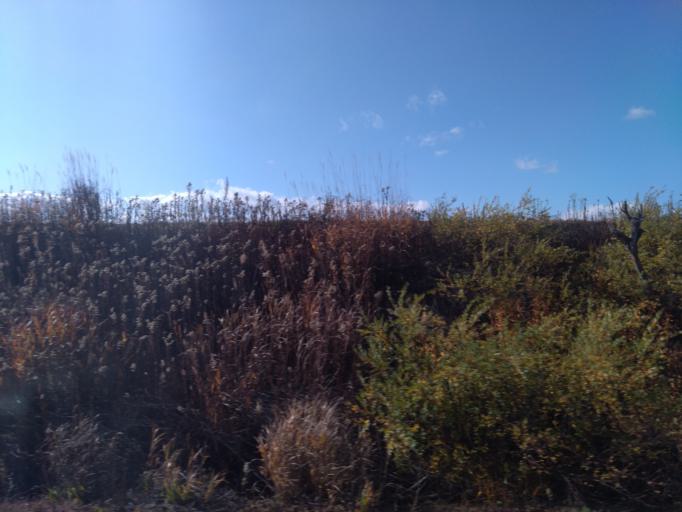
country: JP
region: Hokkaido
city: Kitahiroshima
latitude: 42.9321
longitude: 141.5725
